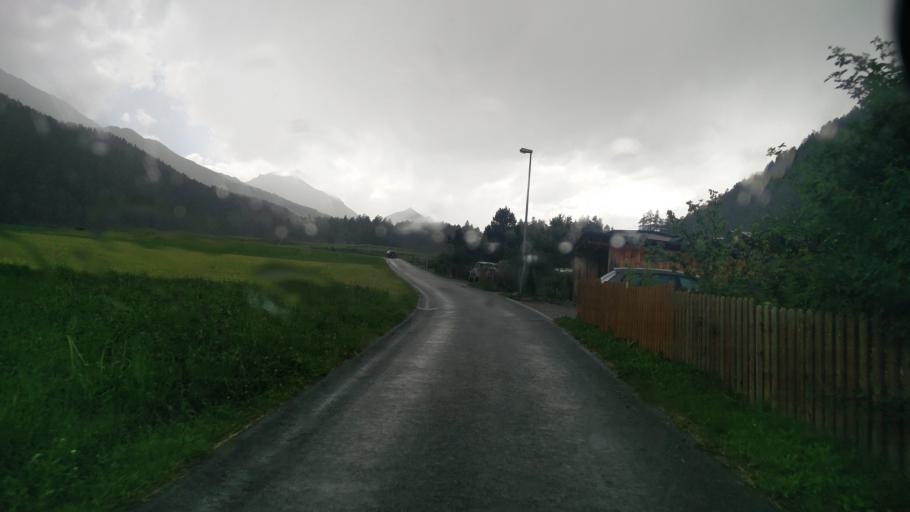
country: IT
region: Trentino-Alto Adige
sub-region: Bolzano
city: Tubre
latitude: 46.6009
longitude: 10.4037
